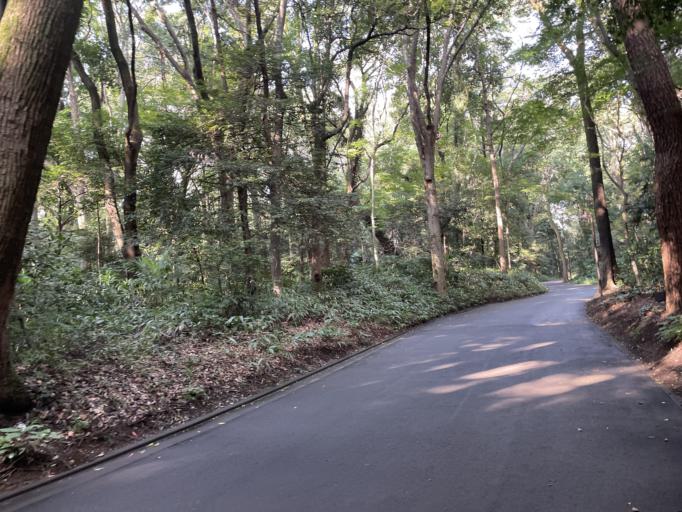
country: JP
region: Tokyo
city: Tokyo
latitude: 35.6784
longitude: 139.7005
